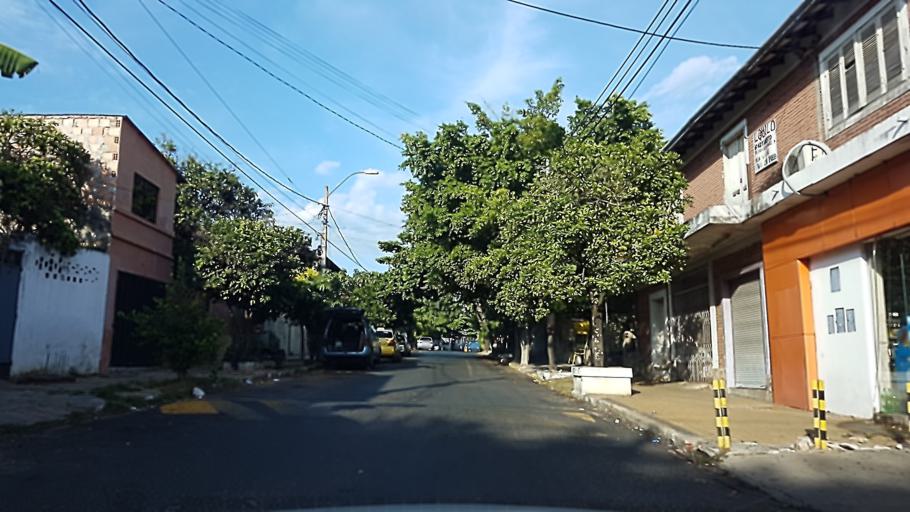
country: PY
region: Asuncion
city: Asuncion
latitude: -25.2826
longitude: -57.6041
